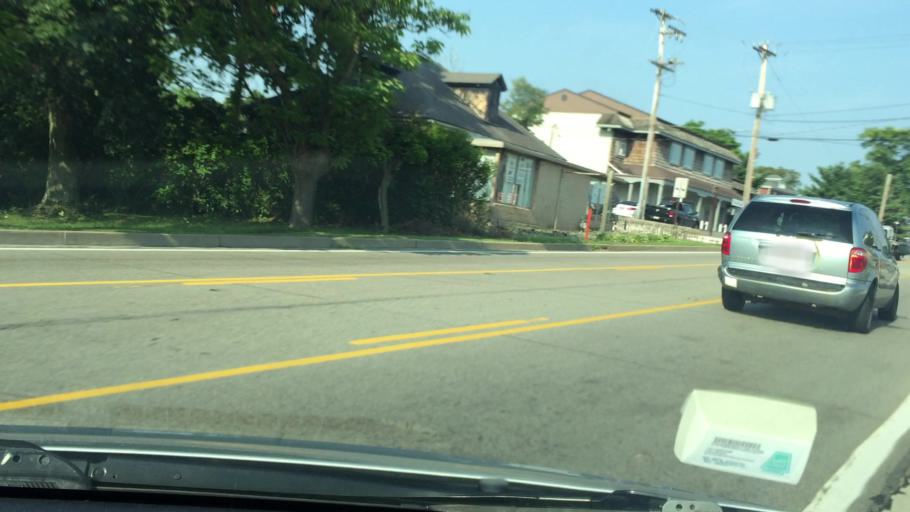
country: US
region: Pennsylvania
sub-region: Allegheny County
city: Rennerdale
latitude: 40.4515
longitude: -80.1301
